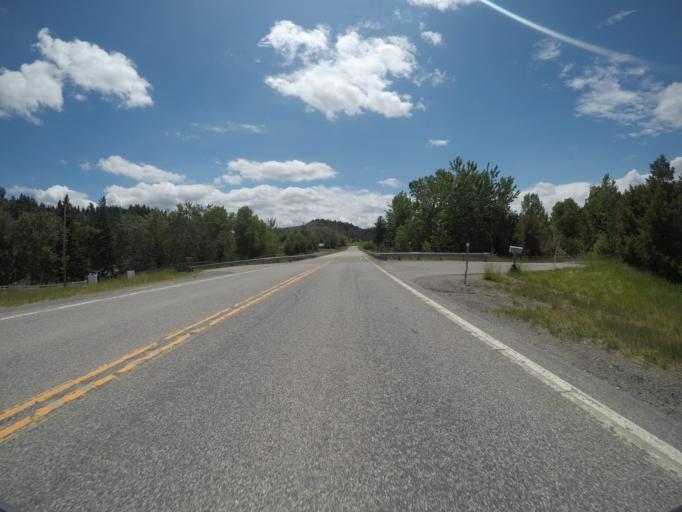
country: US
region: Montana
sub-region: Sweet Grass County
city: Big Timber
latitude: 45.7241
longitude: -109.9968
